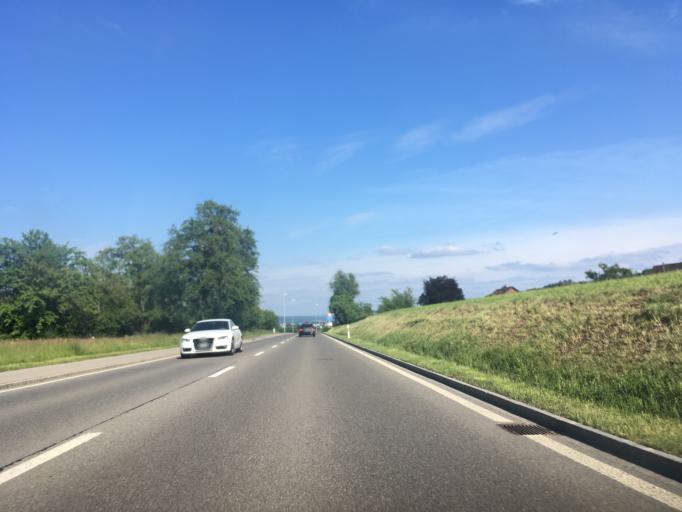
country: CH
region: Zurich
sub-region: Bezirk Dielsdorf
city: Steinmaur
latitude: 47.4928
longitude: 8.4324
